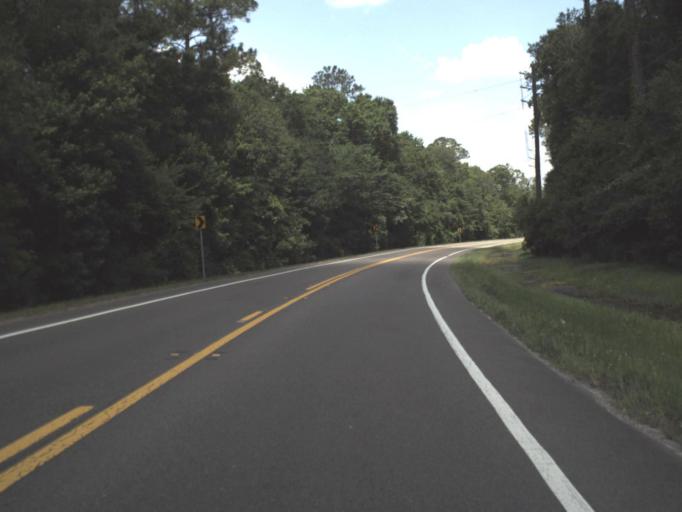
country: US
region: Florida
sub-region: Nassau County
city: Nassau Village-Ratliff
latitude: 30.4879
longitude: -81.7318
